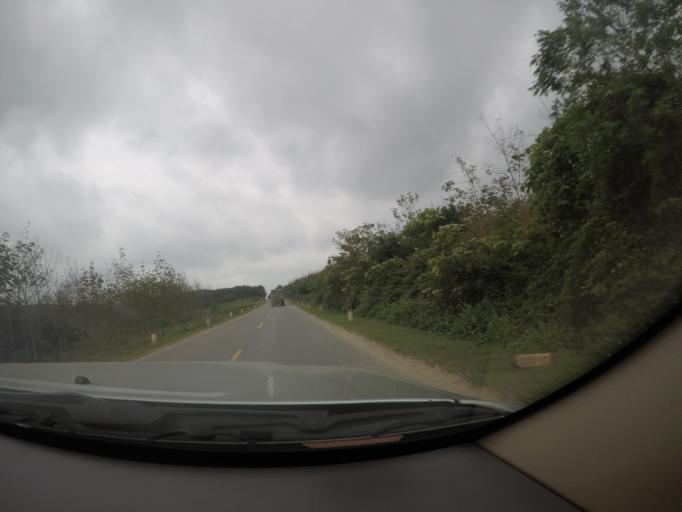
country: VN
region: Quang Binh
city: Kien Giang
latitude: 17.1577
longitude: 106.7461
